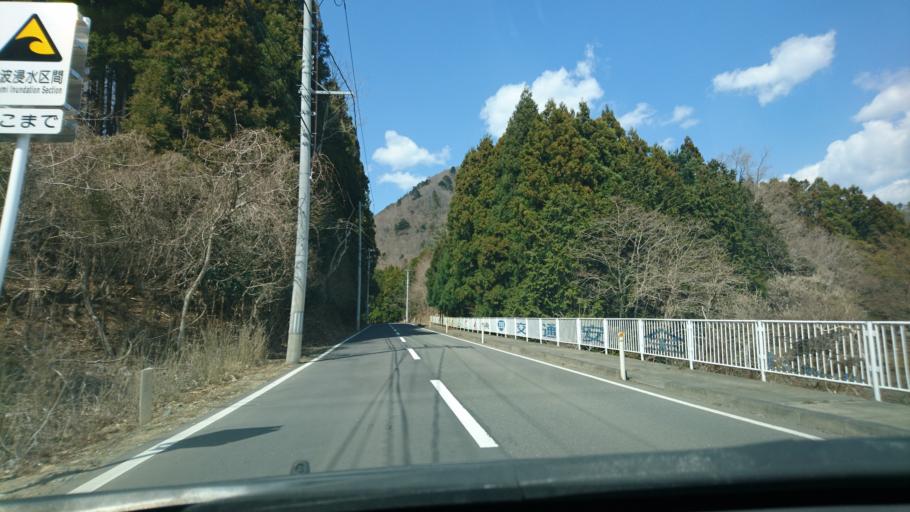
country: JP
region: Miyagi
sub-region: Oshika Gun
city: Onagawa Cho
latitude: 38.4667
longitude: 141.4737
